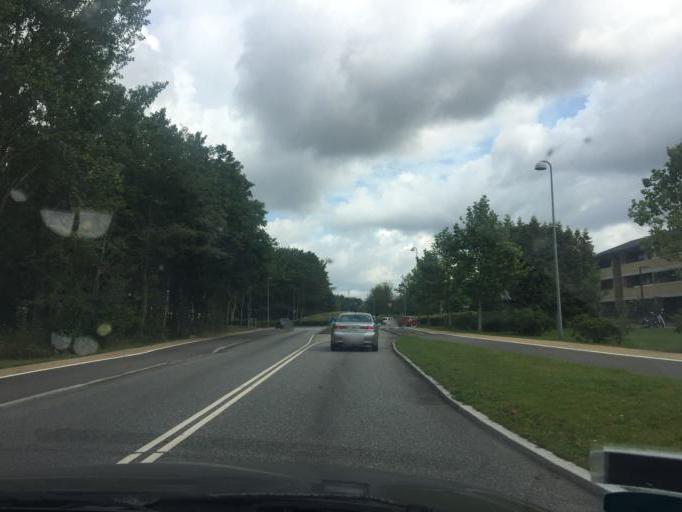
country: DK
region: Capital Region
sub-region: Allerod Kommune
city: Lillerod
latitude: 55.8805
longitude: 12.3511
